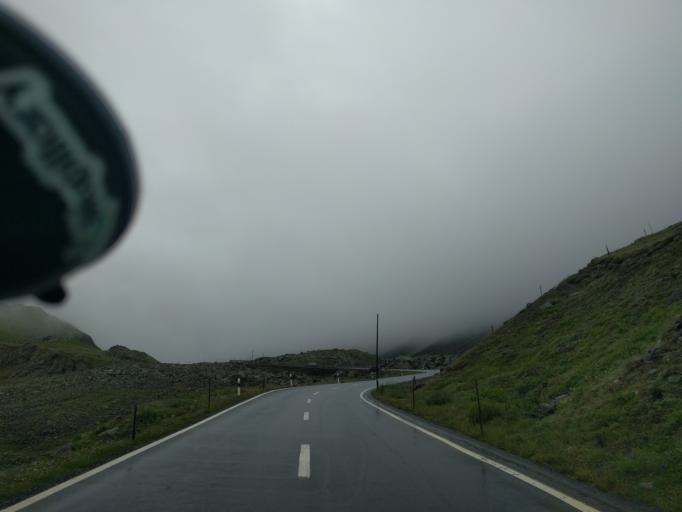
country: CH
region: Grisons
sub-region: Praettigau/Davos District
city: Davos
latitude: 46.7553
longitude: 9.9409
